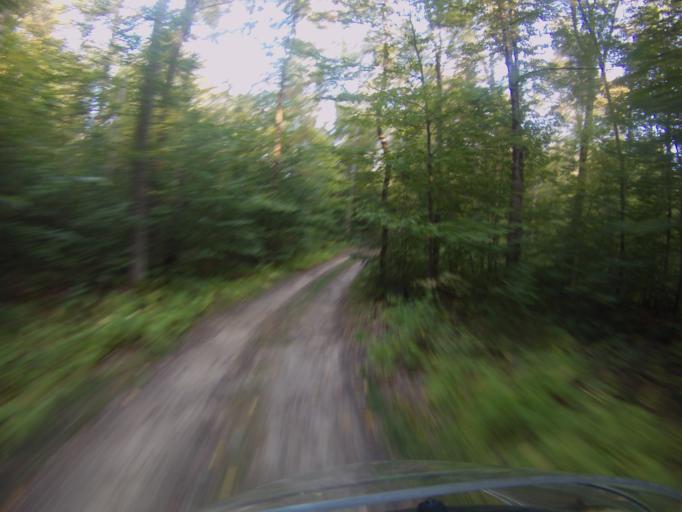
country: US
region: Vermont
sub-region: Addison County
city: Bristol
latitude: 44.0089
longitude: -73.0092
